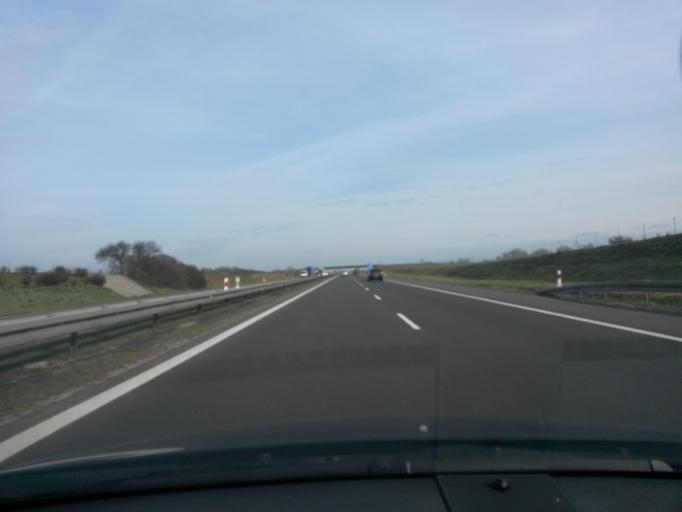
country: PL
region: Greater Poland Voivodeship
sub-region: Powiat poznanski
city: Swarzedz
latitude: 52.3368
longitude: 17.0548
